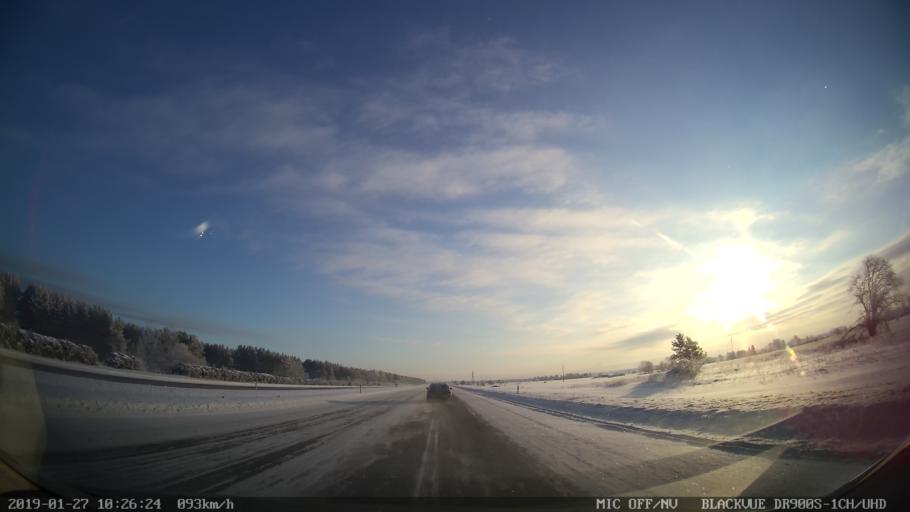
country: EE
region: Harju
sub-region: Maardu linn
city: Maardu
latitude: 59.4468
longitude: 25.0947
